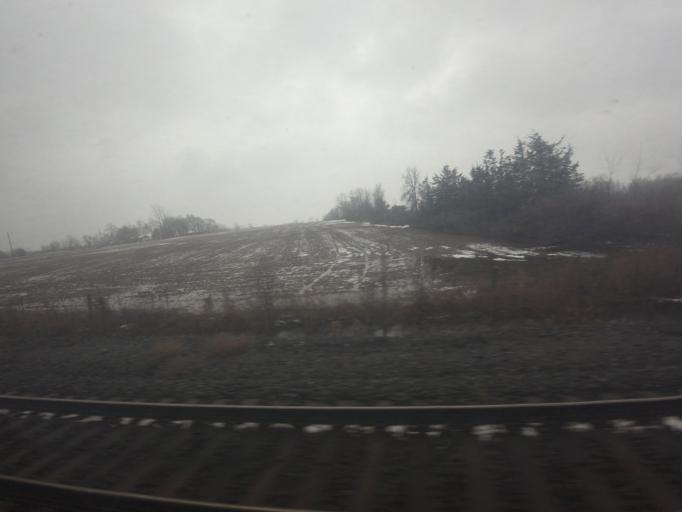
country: CA
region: Ontario
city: Belleville
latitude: 44.2044
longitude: -77.2720
